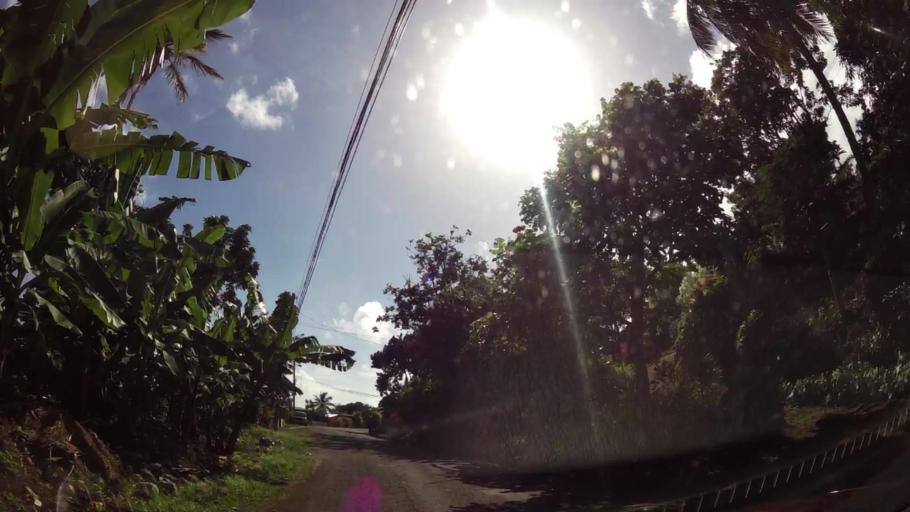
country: DM
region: Saint David
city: Castle Bruce
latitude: 15.4914
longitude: -61.2539
